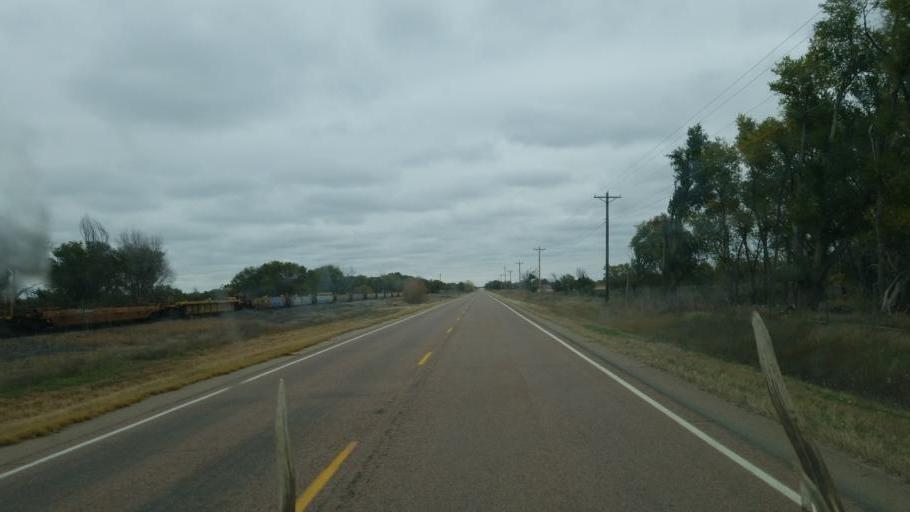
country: US
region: Colorado
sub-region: Otero County
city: Fowler
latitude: 38.1772
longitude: -103.9071
